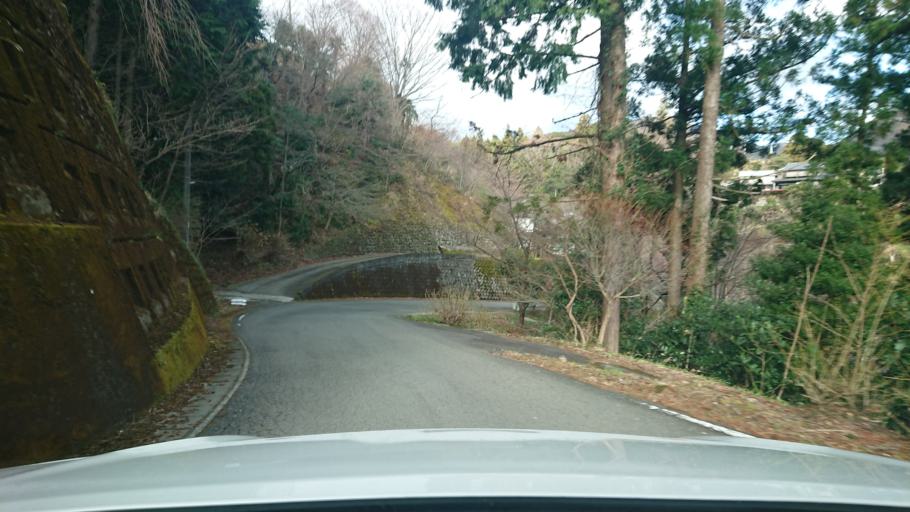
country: JP
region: Tokushima
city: Ishii
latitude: 33.9144
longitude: 134.4073
